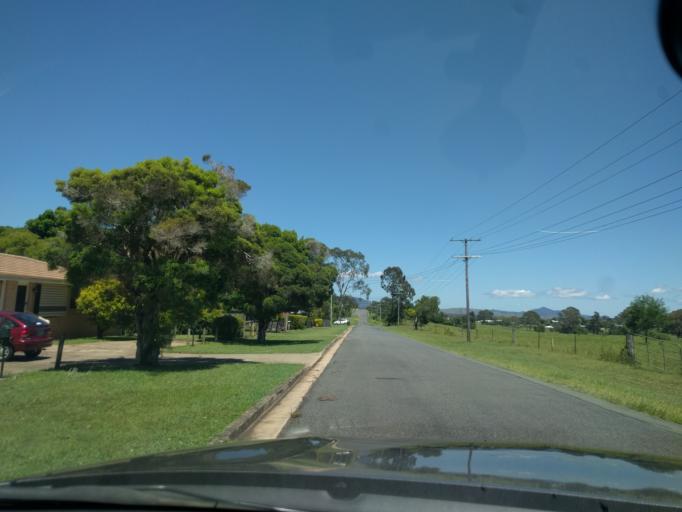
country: AU
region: Queensland
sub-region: Logan
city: Cedar Vale
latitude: -27.9848
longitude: 153.0076
